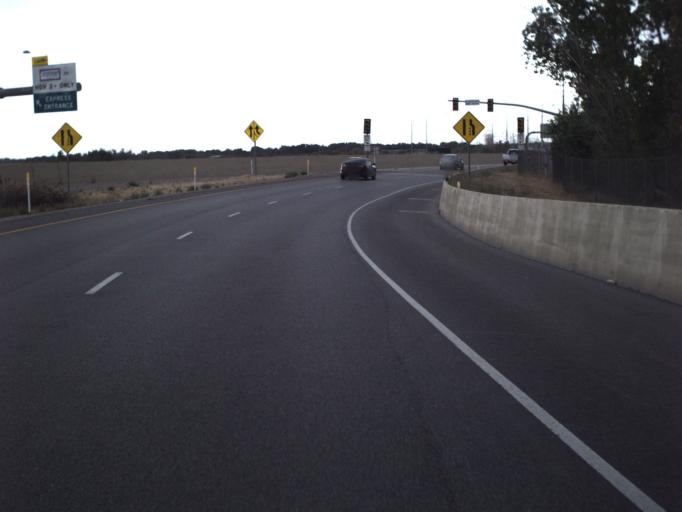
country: US
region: Utah
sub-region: Utah County
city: Springville
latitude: 40.1899
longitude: -111.6457
